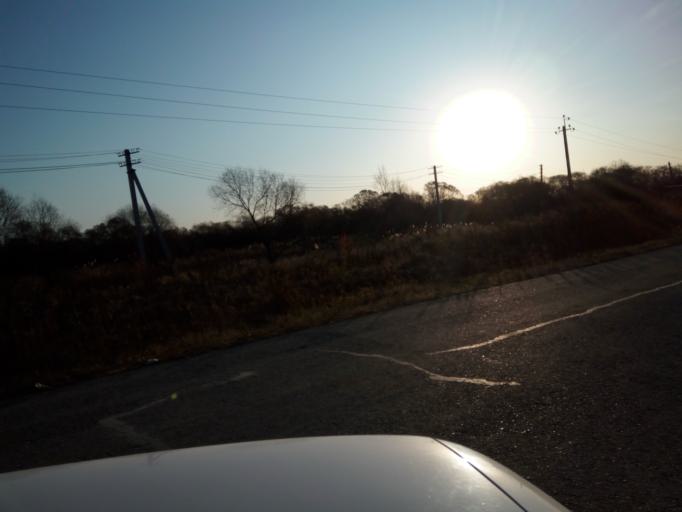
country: RU
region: Primorskiy
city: Lazo
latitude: 45.8577
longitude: 133.6456
